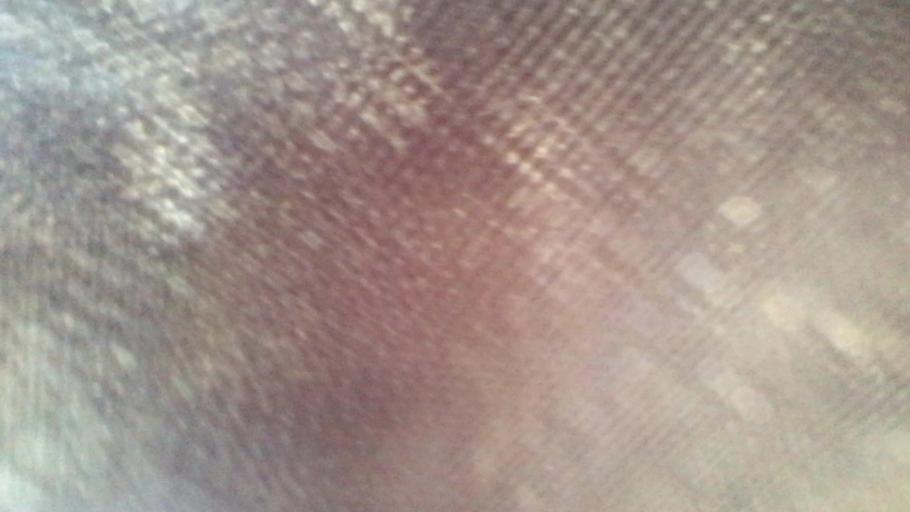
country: US
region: New Jersey
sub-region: Bergen County
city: Cliffside Park
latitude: 40.8100
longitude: -73.9773
